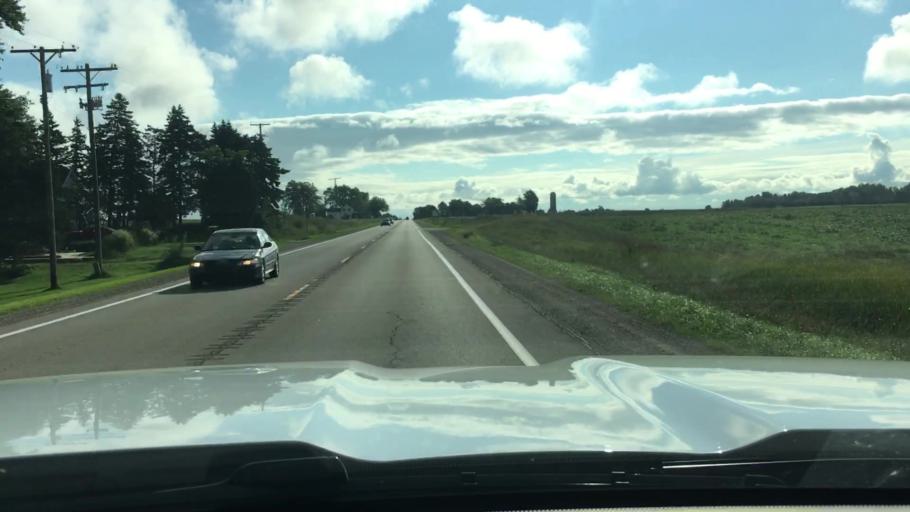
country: US
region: Michigan
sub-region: Tuscola County
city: Cass City
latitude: 43.5998
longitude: -83.2256
